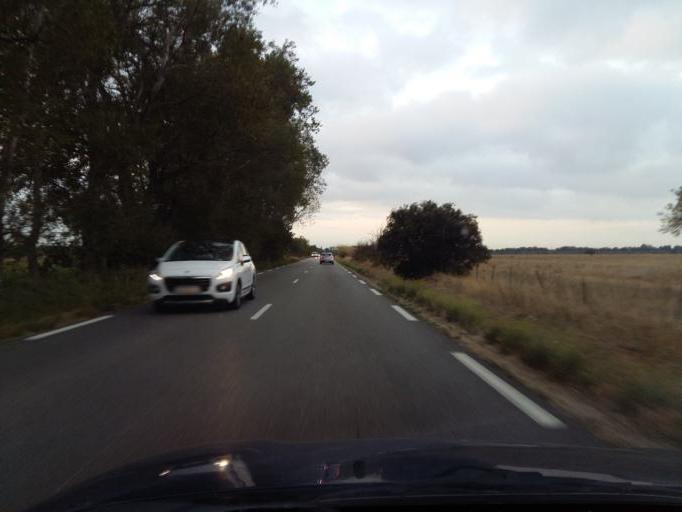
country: FR
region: Provence-Alpes-Cote d'Azur
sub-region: Departement des Bouches-du-Rhone
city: Miramas
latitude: 43.6295
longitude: 5.0183
